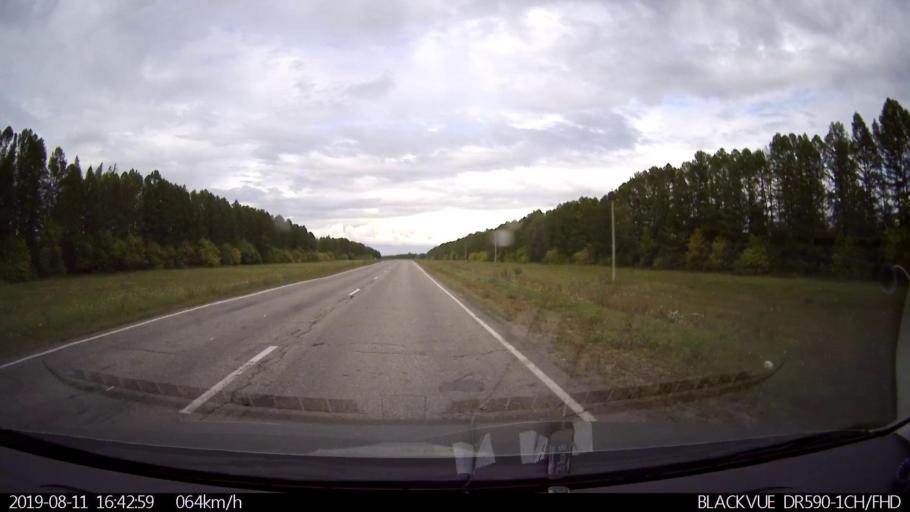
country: RU
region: Ulyanovsk
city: Mayna
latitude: 54.1650
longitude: 47.6676
